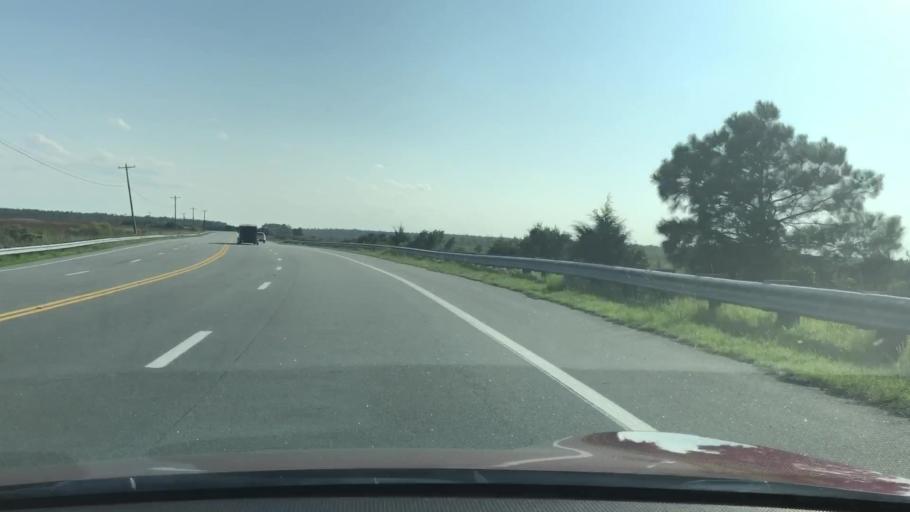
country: US
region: North Carolina
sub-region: Dare County
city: Manteo
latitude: 35.8779
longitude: -75.7789
